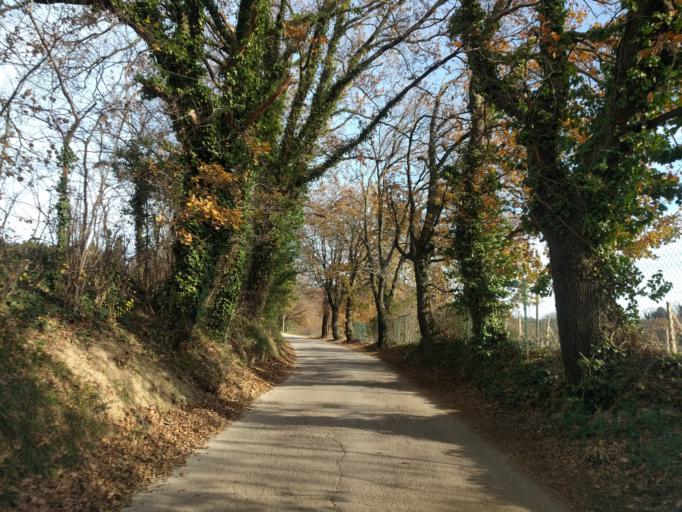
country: IT
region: The Marches
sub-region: Provincia di Pesaro e Urbino
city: Cuccurano
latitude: 43.8142
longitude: 12.9671
